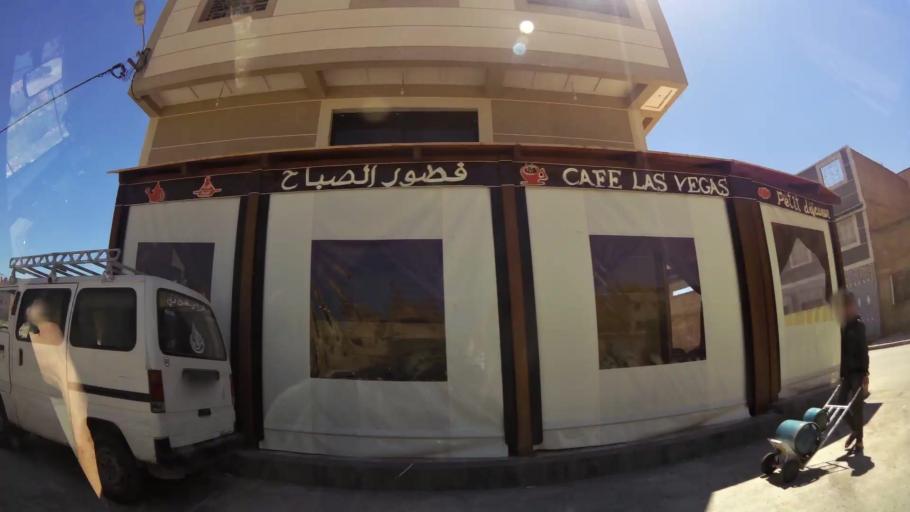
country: MA
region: Oriental
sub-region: Oujda-Angad
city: Oujda
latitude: 34.6607
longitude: -1.8830
